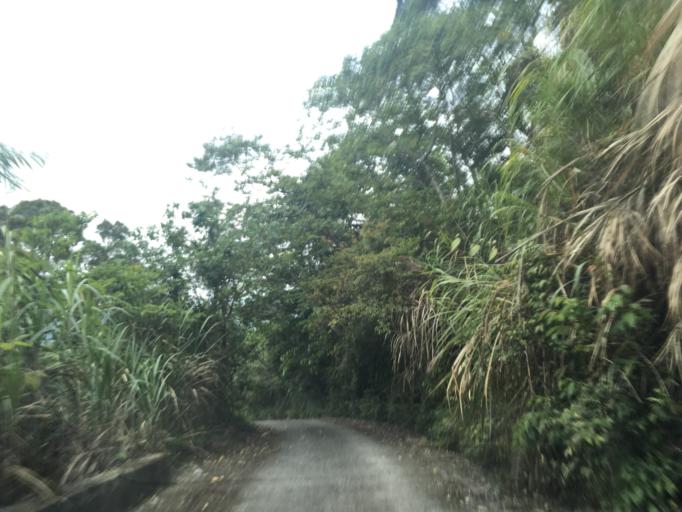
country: TW
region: Taiwan
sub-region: Taichung City
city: Taichung
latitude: 24.1447
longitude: 120.8219
